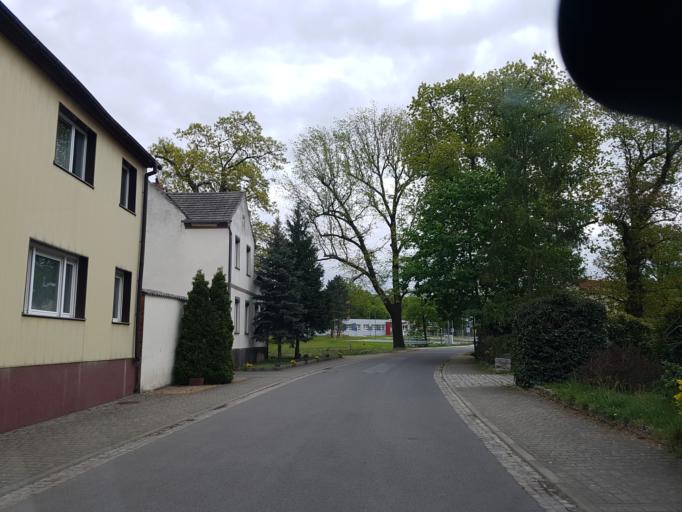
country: DE
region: Brandenburg
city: Altdobern
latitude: 51.6501
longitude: 14.0383
